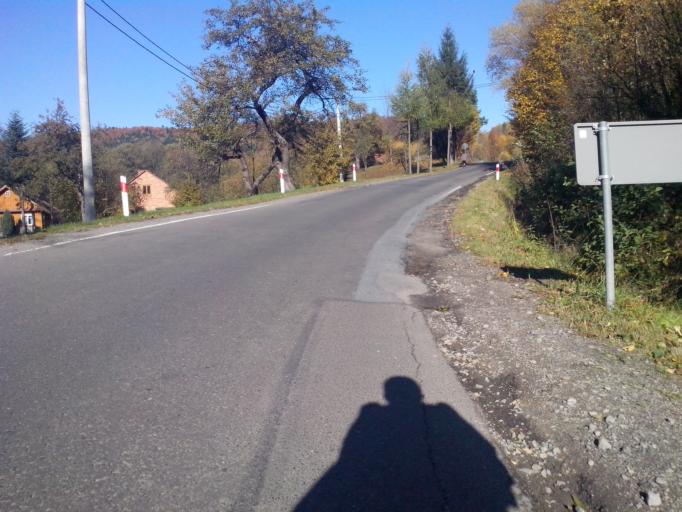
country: PL
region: Subcarpathian Voivodeship
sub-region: Powiat krosnienski
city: Korczyna
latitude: 49.7656
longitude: 21.7996
